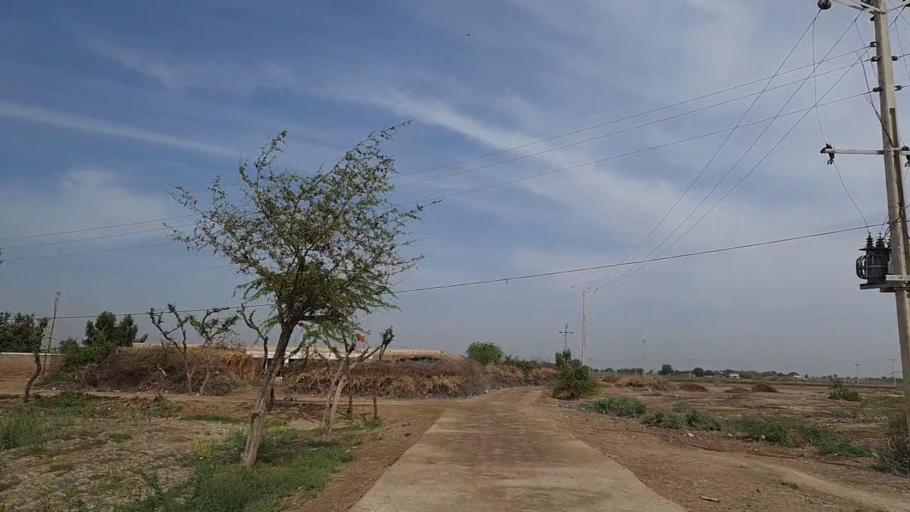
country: PK
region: Sindh
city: Samaro
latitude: 25.2928
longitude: 69.4124
